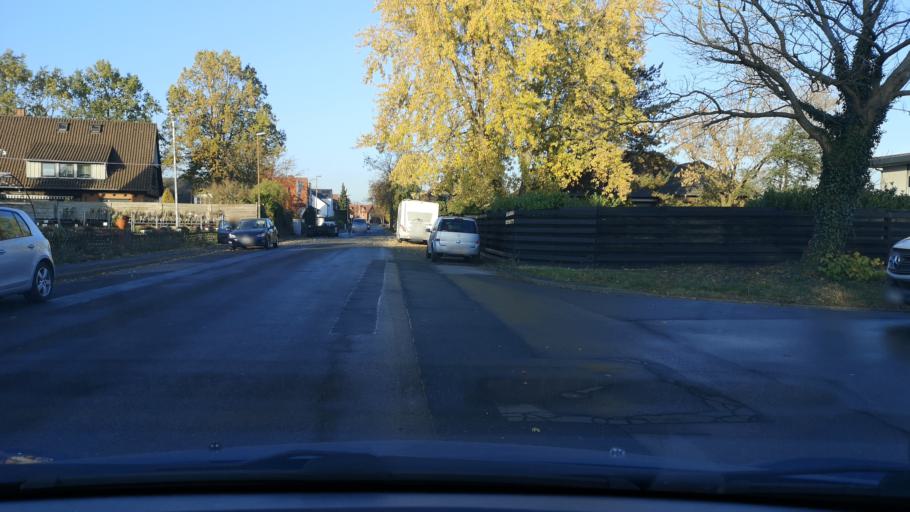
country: DE
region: Lower Saxony
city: Langenhagen
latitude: 52.4514
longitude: 9.7884
